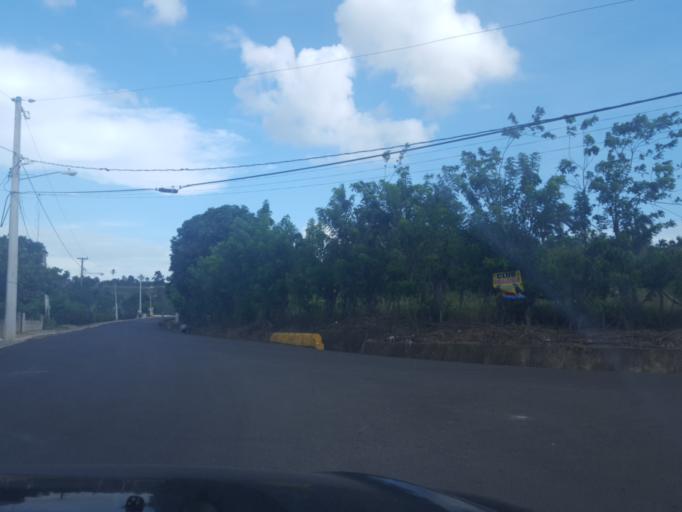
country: DO
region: Santiago
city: Baitoa
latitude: 19.3586
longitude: -70.6337
